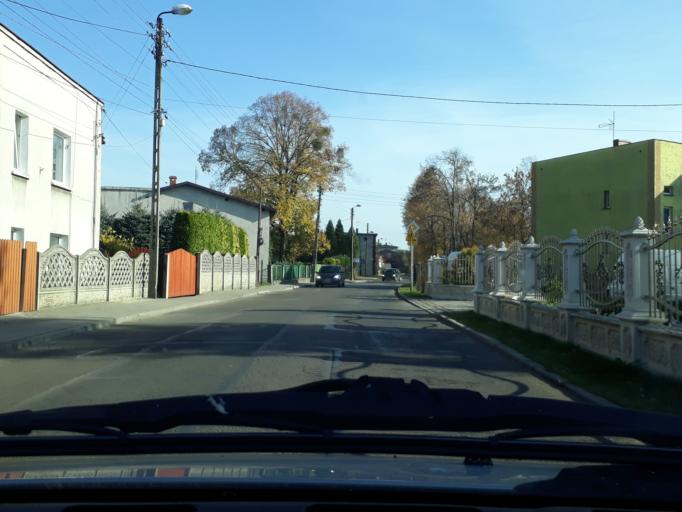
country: PL
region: Silesian Voivodeship
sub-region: Powiat tarnogorski
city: Tarnowskie Gory
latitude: 50.4242
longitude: 18.8628
